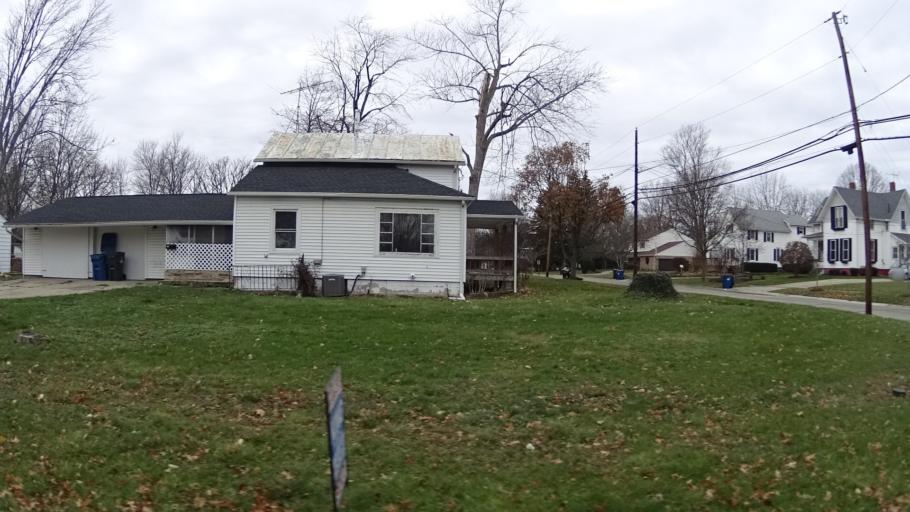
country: US
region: Ohio
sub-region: Lorain County
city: Wellington
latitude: 41.1614
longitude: -82.2152
